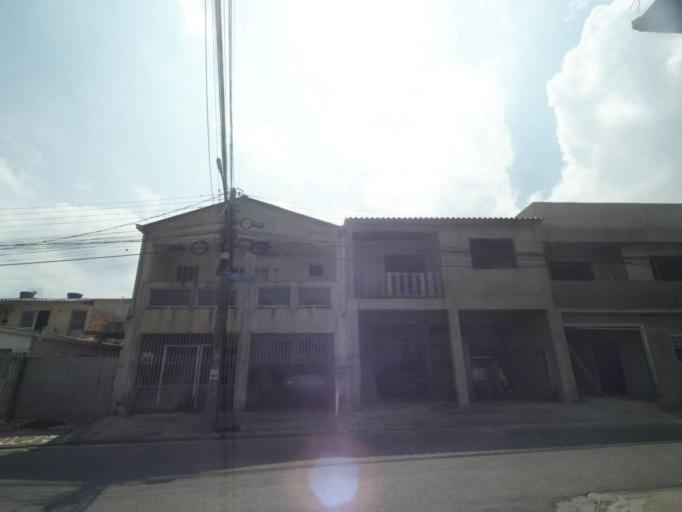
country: BR
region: Parana
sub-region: Curitiba
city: Curitiba
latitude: -25.5012
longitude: -49.3500
